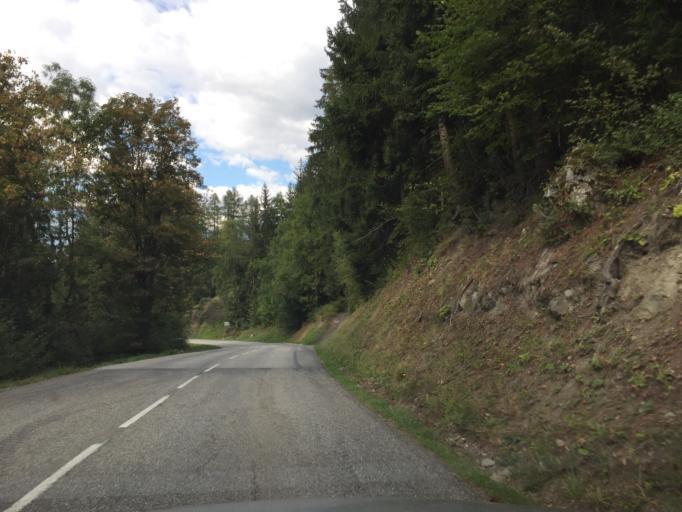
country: FR
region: Rhone-Alpes
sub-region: Departement de la Savoie
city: Belle-Plagne
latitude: 45.5546
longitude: 6.7495
